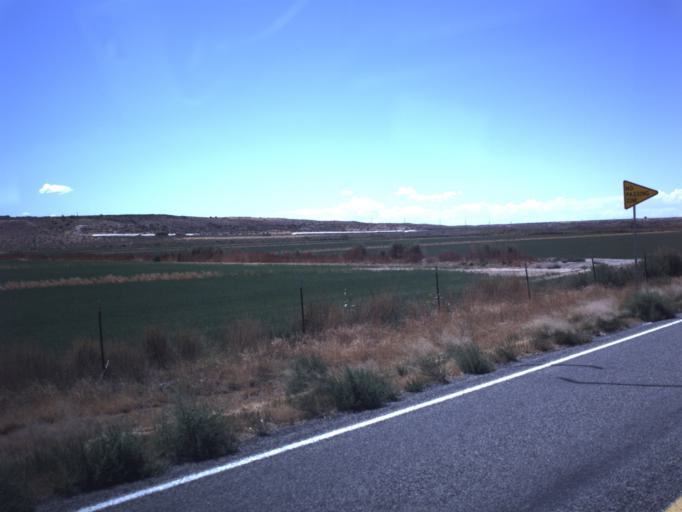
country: US
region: Utah
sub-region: Millard County
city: Delta
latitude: 39.5318
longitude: -112.3342
